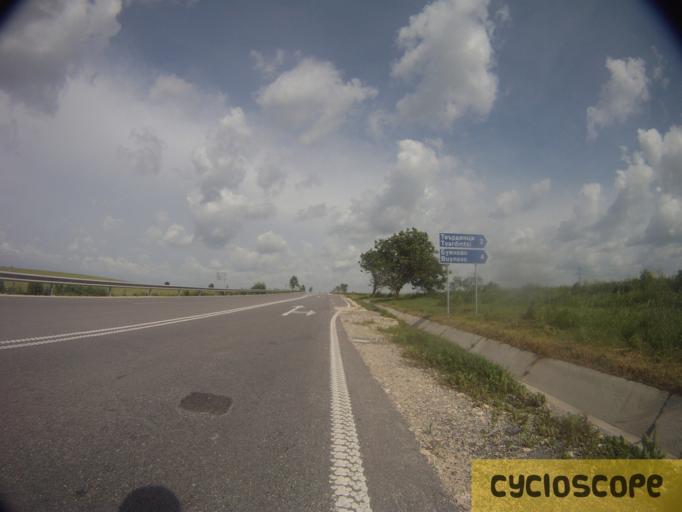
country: BG
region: Razgrad
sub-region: Obshtina Samuil
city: Samuil
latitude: 43.3963
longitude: 26.7847
